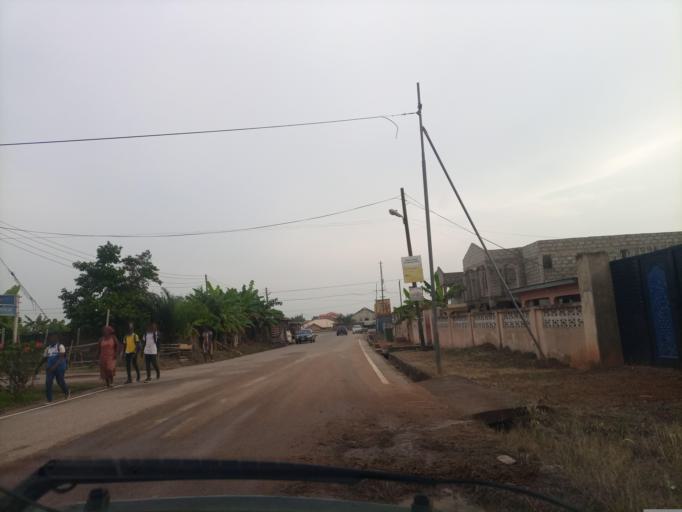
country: GH
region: Western
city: Takoradi
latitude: 4.9286
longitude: -1.7828
